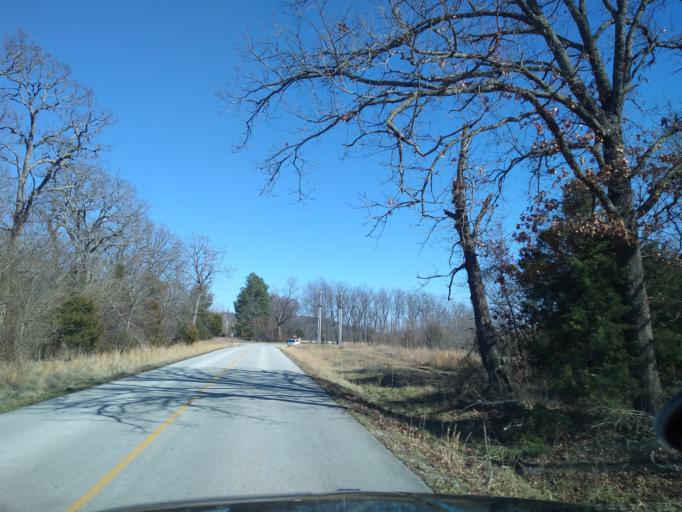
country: US
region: Arkansas
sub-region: Washington County
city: Farmington
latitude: 36.0573
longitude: -94.2374
